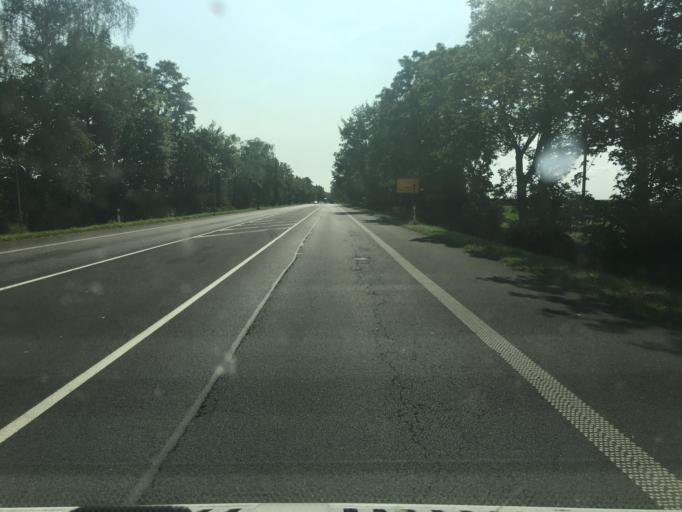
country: DE
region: North Rhine-Westphalia
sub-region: Regierungsbezirk Koln
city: Norvenich
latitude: 50.7514
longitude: 6.6467
